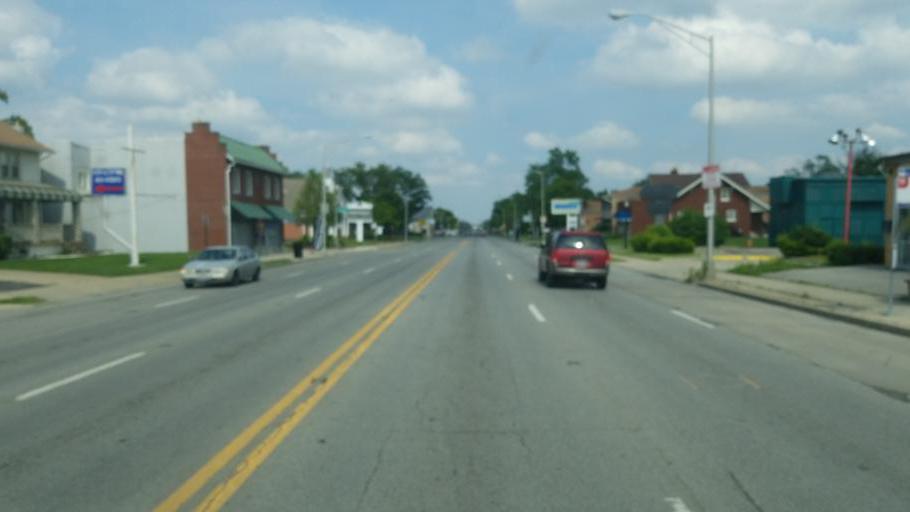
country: US
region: Ohio
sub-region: Franklin County
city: Upper Arlington
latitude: 39.9545
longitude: -83.0827
